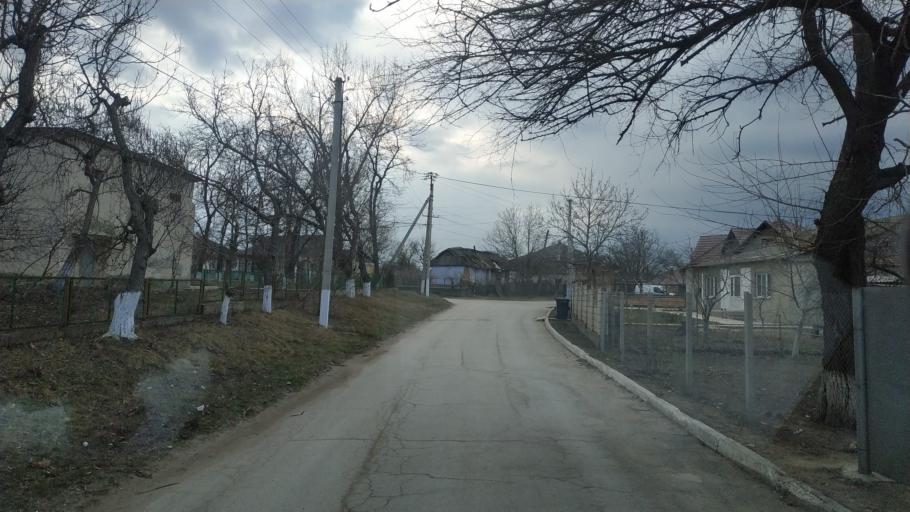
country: MD
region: Anenii Noi
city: Anenii Noi
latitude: 46.8852
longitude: 29.3101
